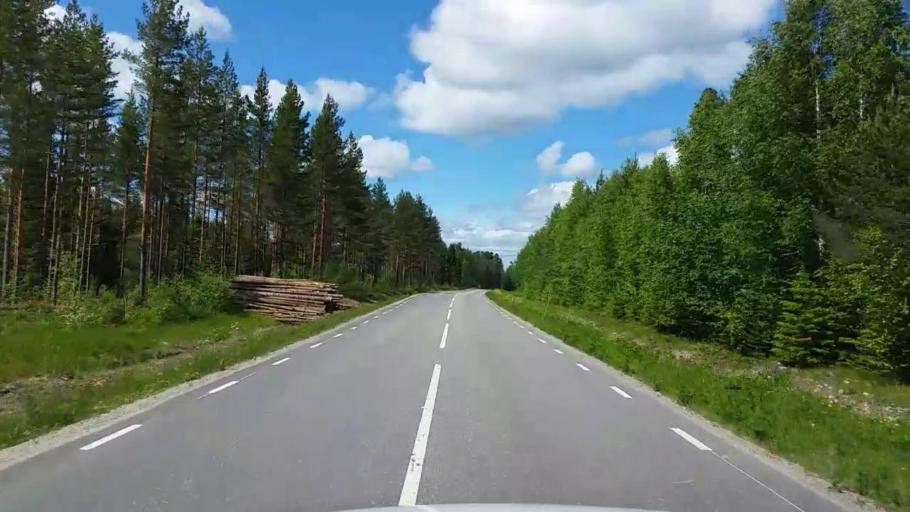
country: SE
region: Gaevleborg
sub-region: Ovanakers Kommun
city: Alfta
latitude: 61.2645
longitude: 16.1223
